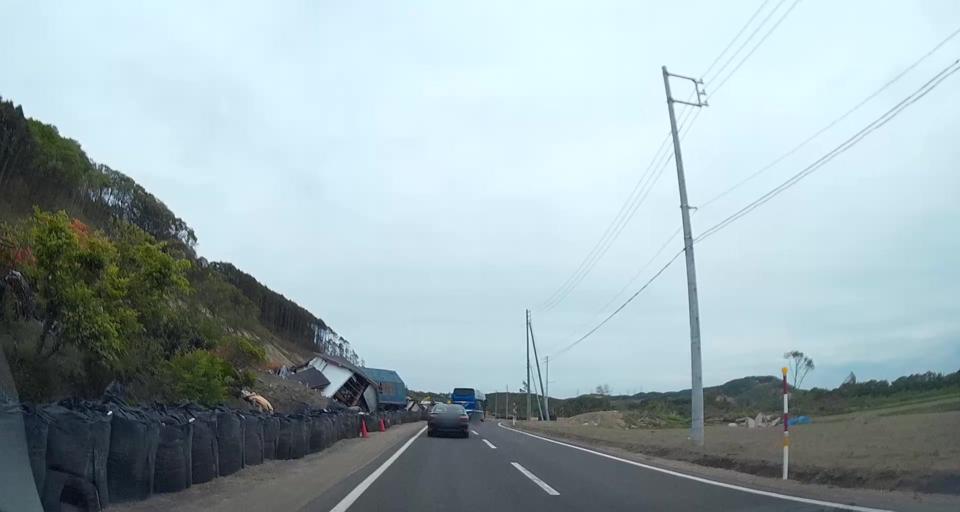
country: JP
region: Hokkaido
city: Chitose
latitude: 42.7499
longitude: 141.9123
